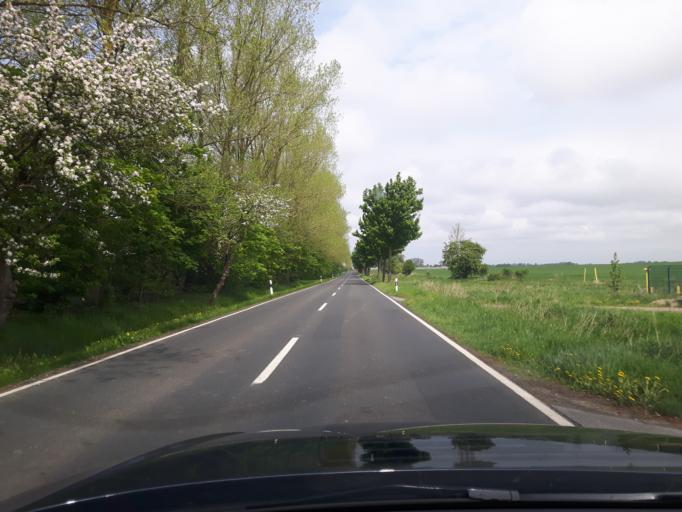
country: DE
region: Mecklenburg-Vorpommern
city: Barth
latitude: 54.2794
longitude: 12.7176
